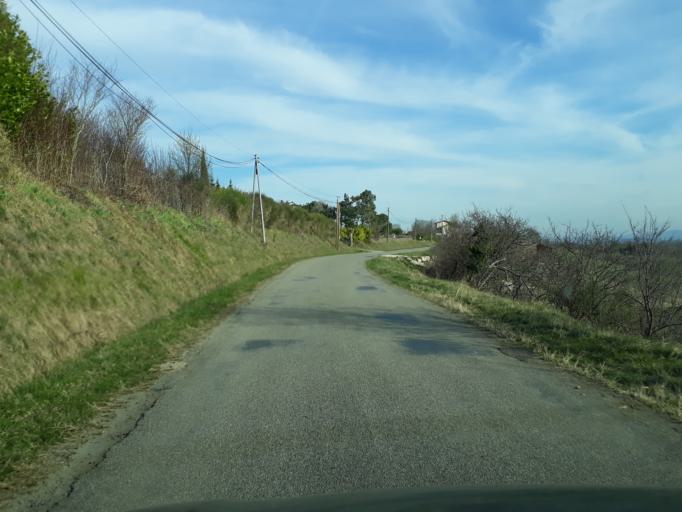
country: FR
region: Midi-Pyrenees
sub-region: Departement de la Haute-Garonne
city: Montesquieu-Volvestre
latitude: 43.1798
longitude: 1.3161
